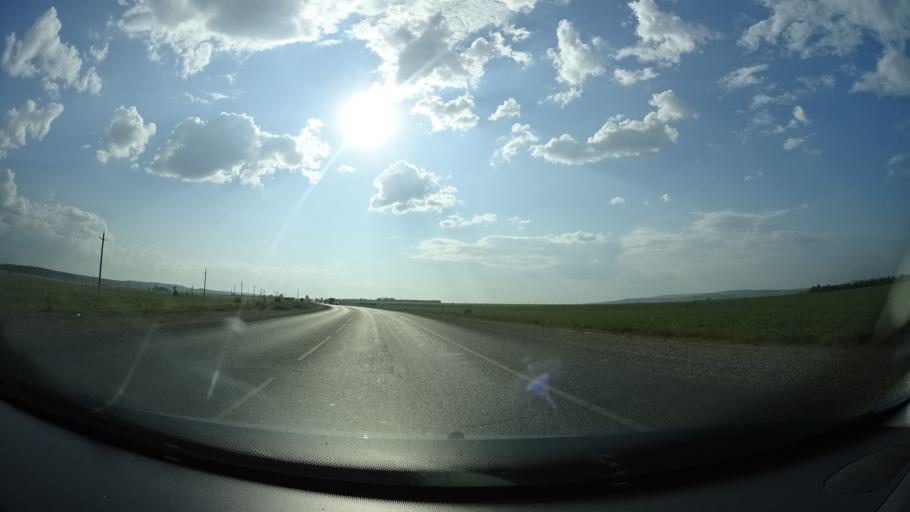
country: RU
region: Bashkortostan
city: Oktyabr'skiy
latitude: 54.4822
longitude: 53.3834
